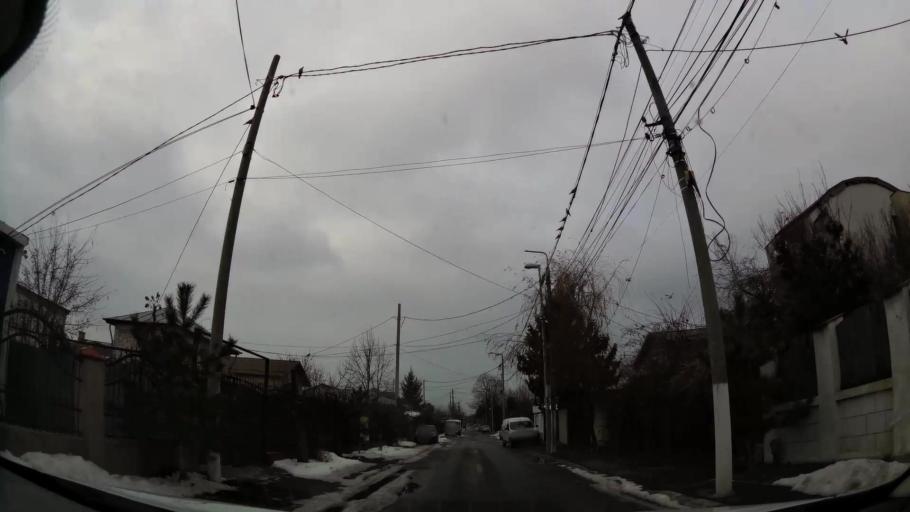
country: RO
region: Ilfov
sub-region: Voluntari City
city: Voluntari
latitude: 44.4986
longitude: 26.1990
